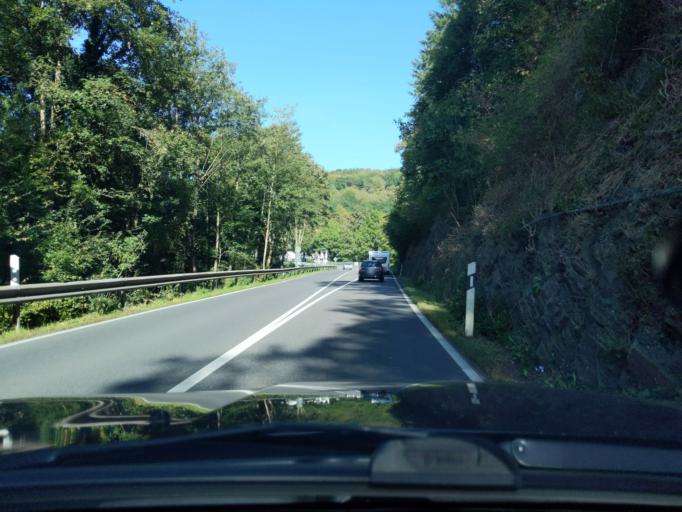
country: DE
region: North Rhine-Westphalia
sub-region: Regierungsbezirk Koln
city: Eitorf
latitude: 50.7631
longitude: 7.4016
